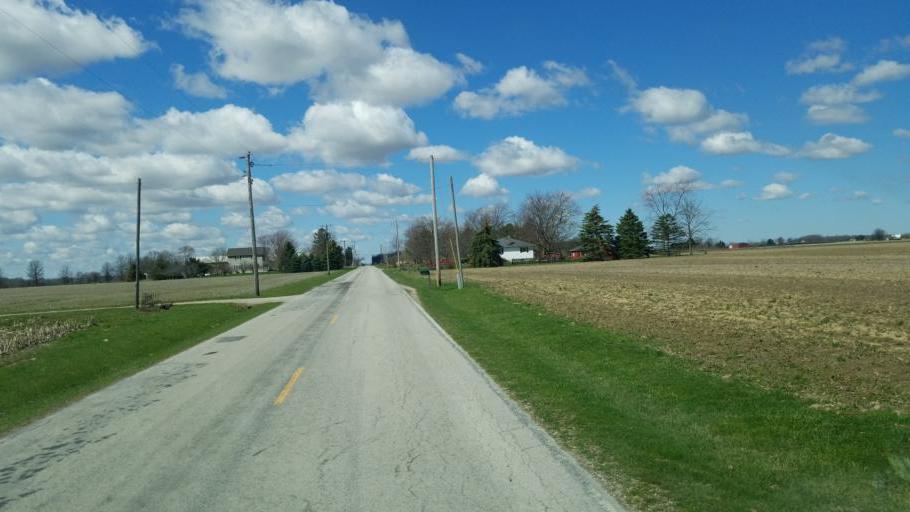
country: US
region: Ohio
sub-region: Sandusky County
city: Mount Carmel
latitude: 41.2417
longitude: -82.9620
